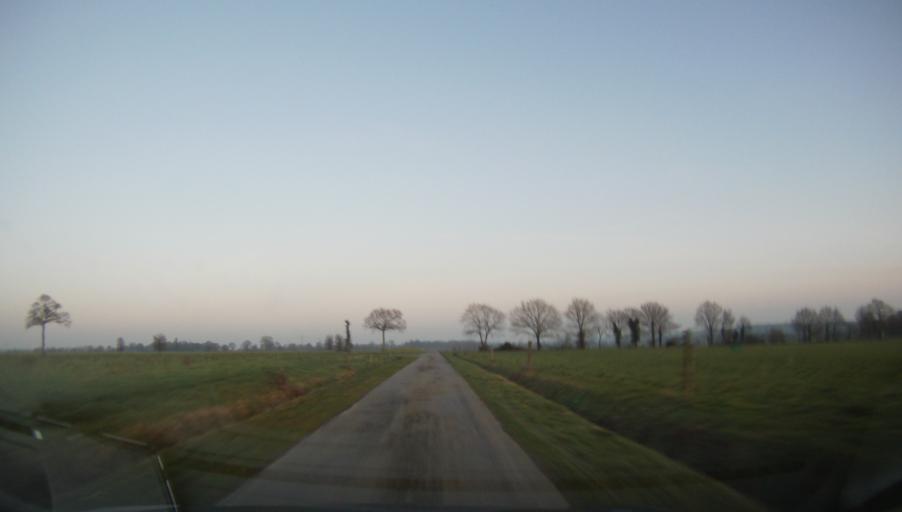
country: FR
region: Brittany
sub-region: Departement d'Ille-et-Vilaine
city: Crevin
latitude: 47.9311
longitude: -1.6465
